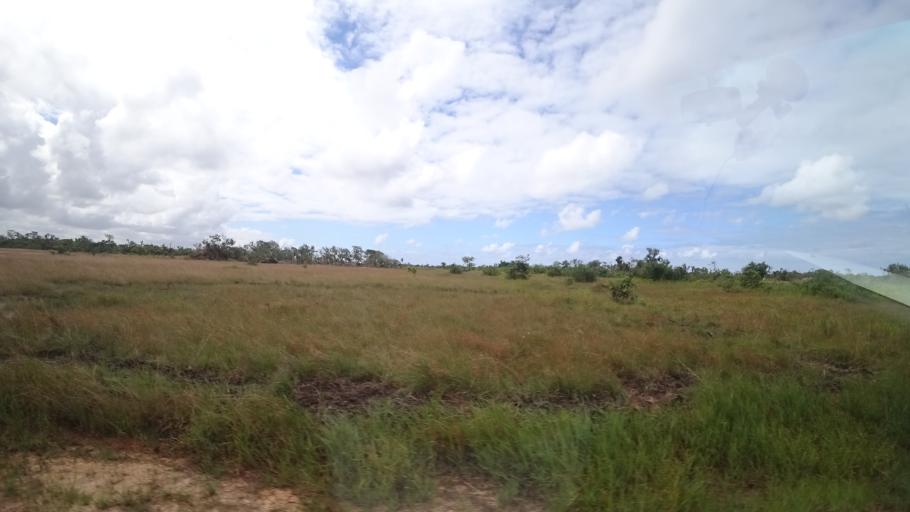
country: MZ
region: Sofala
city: Beira
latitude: -19.6118
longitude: 35.2144
